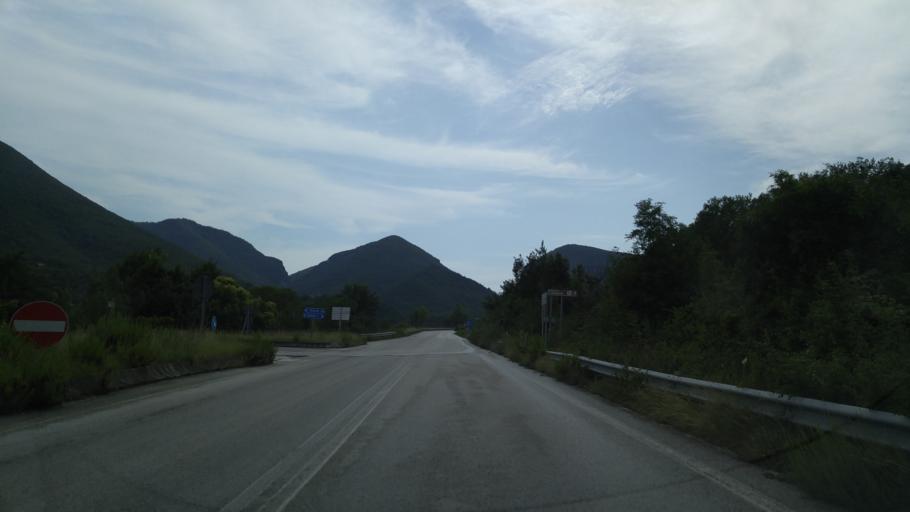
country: IT
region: The Marches
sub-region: Provincia di Pesaro e Urbino
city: Fossombrone
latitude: 43.6665
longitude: 12.7557
